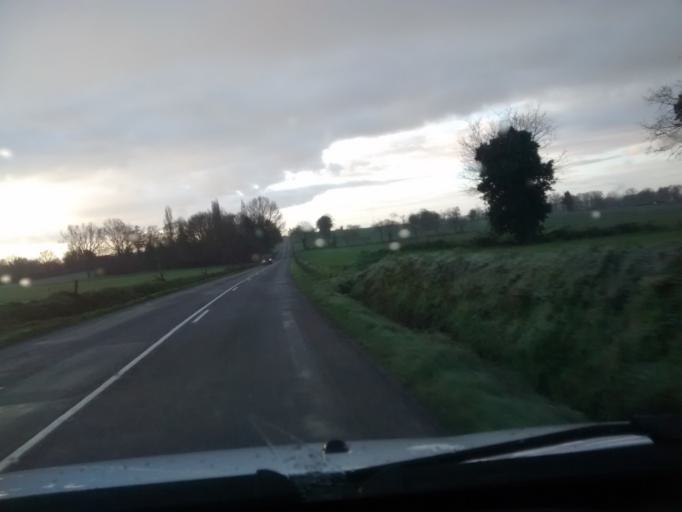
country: FR
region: Brittany
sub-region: Departement d'Ille-et-Vilaine
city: Domalain
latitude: 47.9750
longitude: -1.2698
